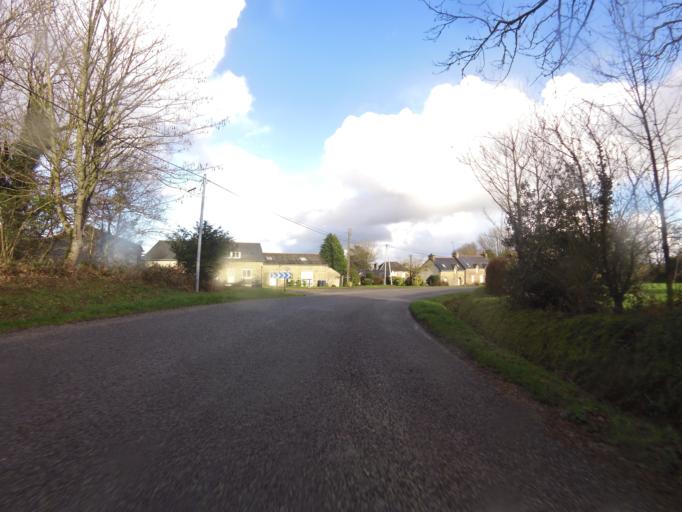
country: FR
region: Brittany
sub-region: Departement des Cotes-d'Armor
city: Rostrenen
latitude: 48.1789
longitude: -3.2851
